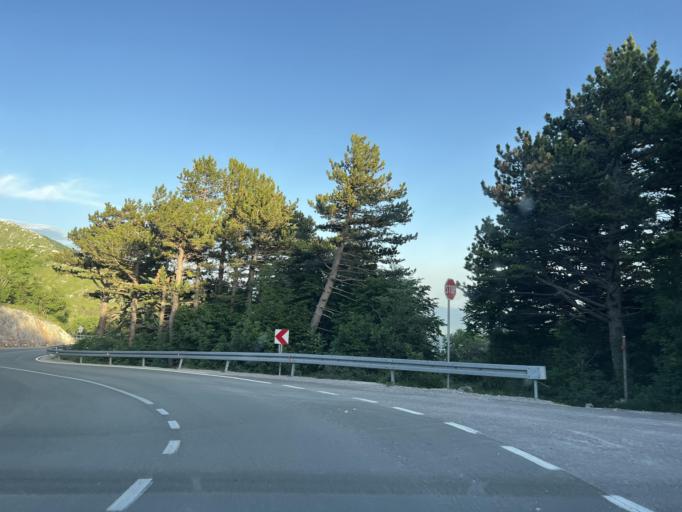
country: HR
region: Primorsko-Goranska
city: Podhum
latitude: 45.3973
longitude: 14.5489
